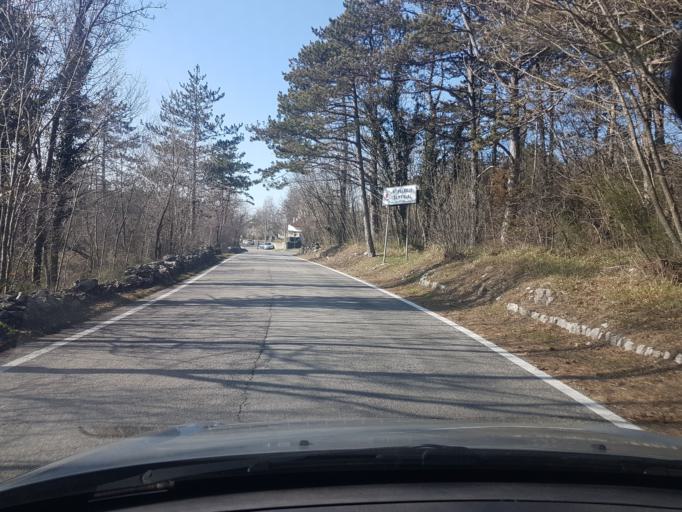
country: IT
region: Friuli Venezia Giulia
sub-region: Provincia di Trieste
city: Aurisina
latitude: 45.7686
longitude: 13.6940
